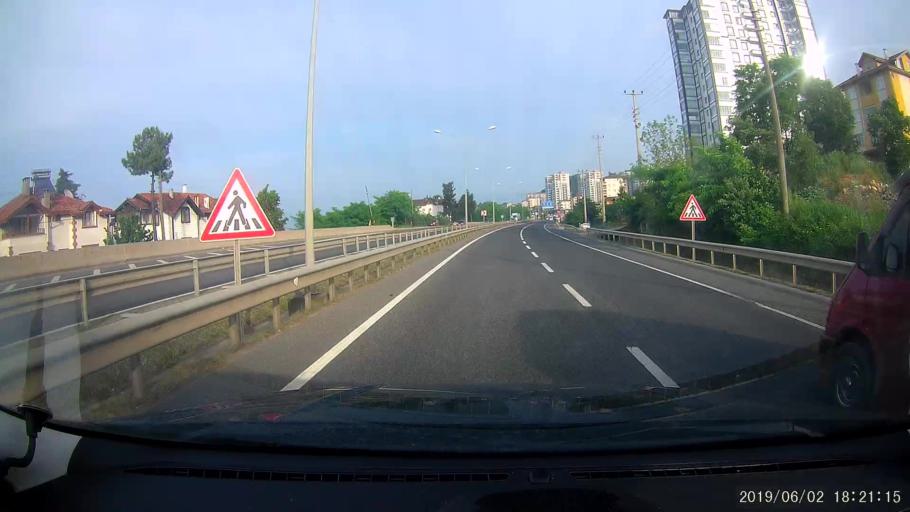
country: TR
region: Ordu
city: Fatsa
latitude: 41.0671
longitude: 37.4664
